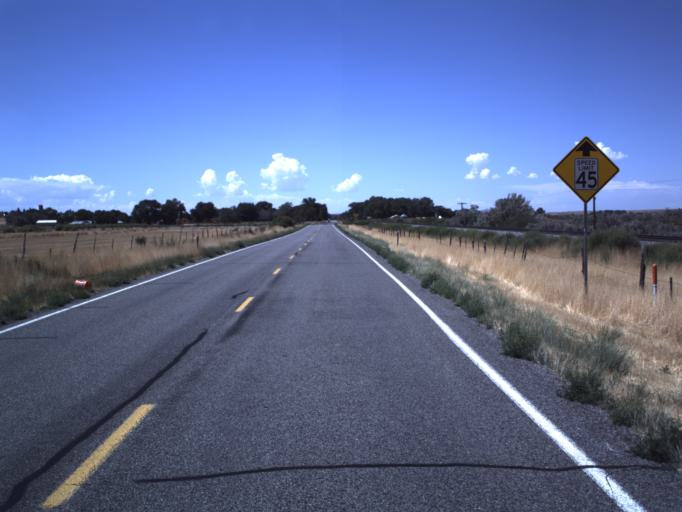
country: US
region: Utah
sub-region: Millard County
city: Delta
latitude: 39.5371
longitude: -112.2652
